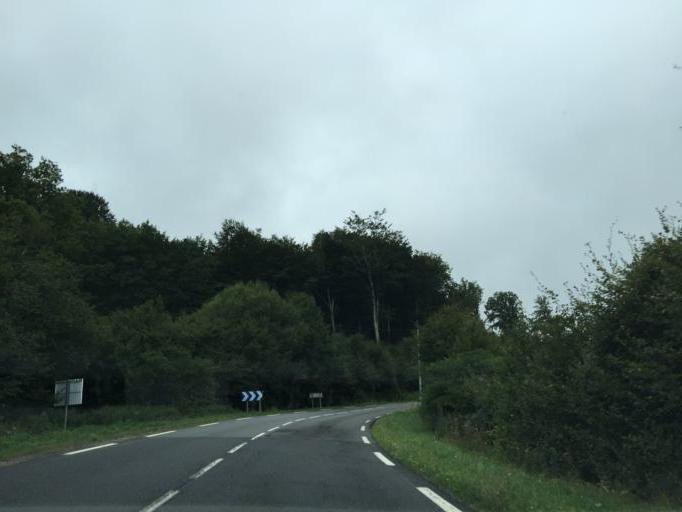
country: FR
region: Midi-Pyrenees
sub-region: Departement de l'Aveyron
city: Salles-Curan
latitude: 44.2404
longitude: 2.8984
